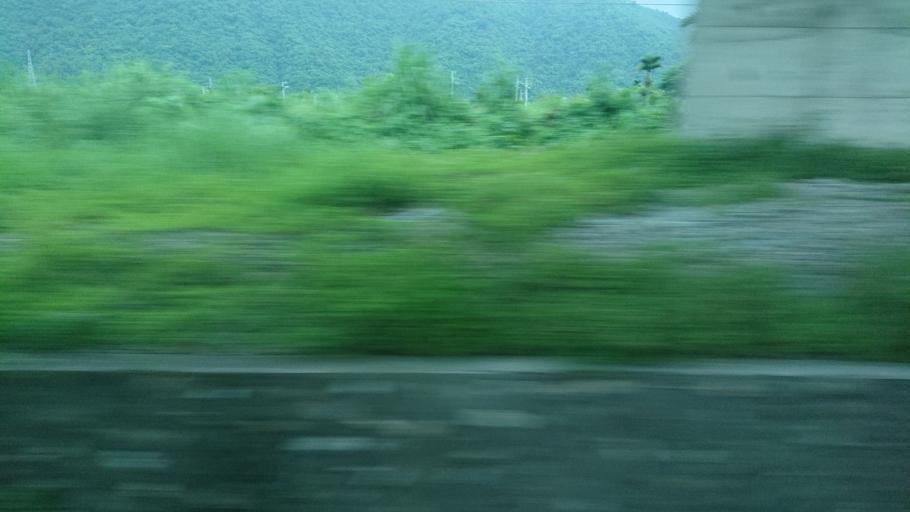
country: TW
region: Taiwan
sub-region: Hualien
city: Hualian
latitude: 24.1217
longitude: 121.6364
